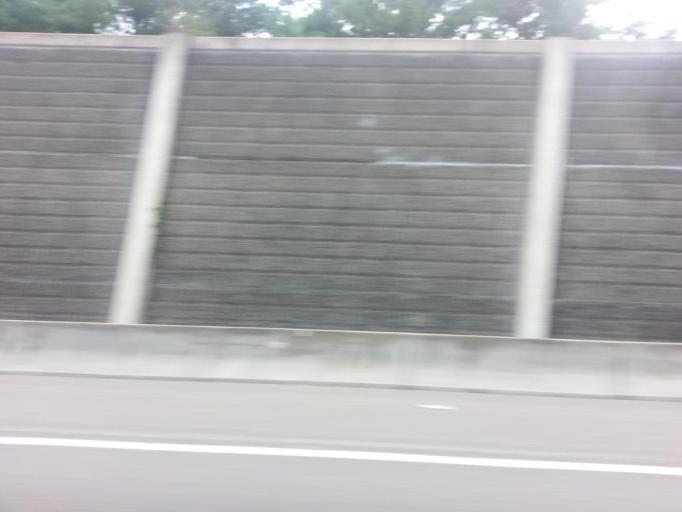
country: US
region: Tennessee
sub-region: Sullivan County
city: Fairmount
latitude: 36.6249
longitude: -82.1409
